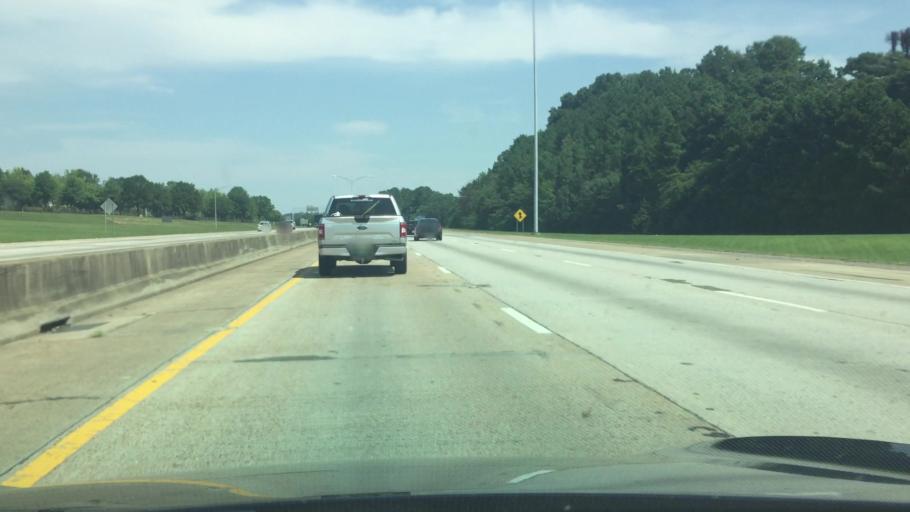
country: US
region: Alabama
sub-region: Jefferson County
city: Homewood
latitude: 33.4505
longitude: -86.8180
